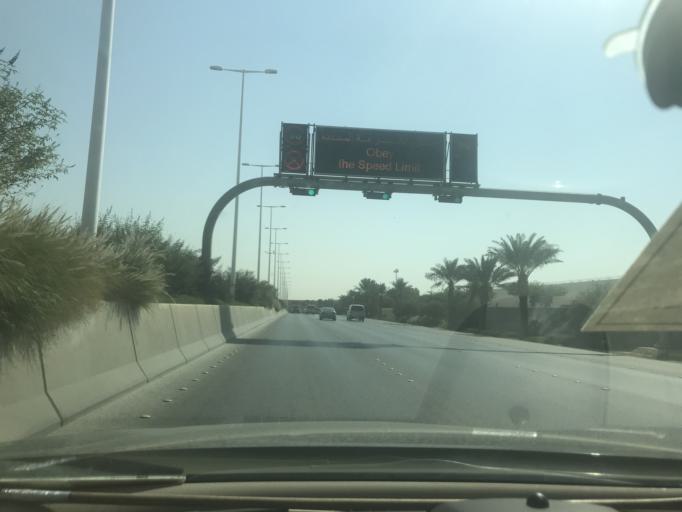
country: SA
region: Ar Riyad
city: Riyadh
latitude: 24.7146
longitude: 46.7174
